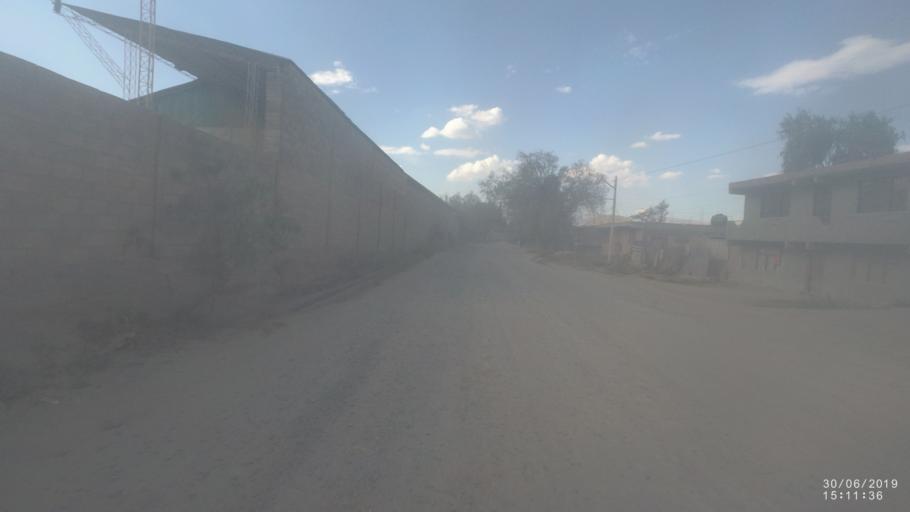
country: BO
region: Cochabamba
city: Irpa Irpa
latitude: -17.7273
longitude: -66.2912
